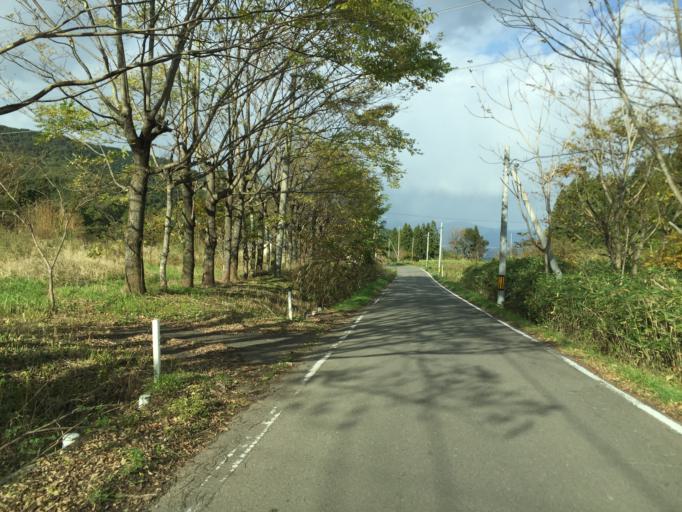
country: JP
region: Fukushima
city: Fukushima-shi
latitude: 37.7100
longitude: 140.3412
